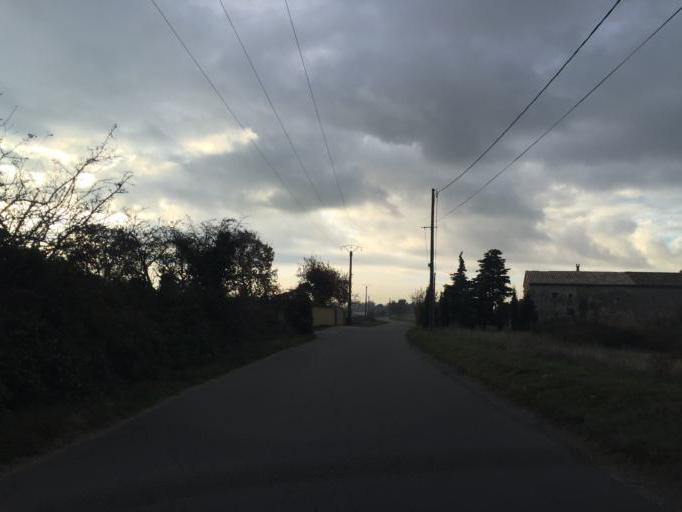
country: FR
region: Provence-Alpes-Cote d'Azur
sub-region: Departement du Vaucluse
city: Jonquieres
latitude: 44.1229
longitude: 4.8763
